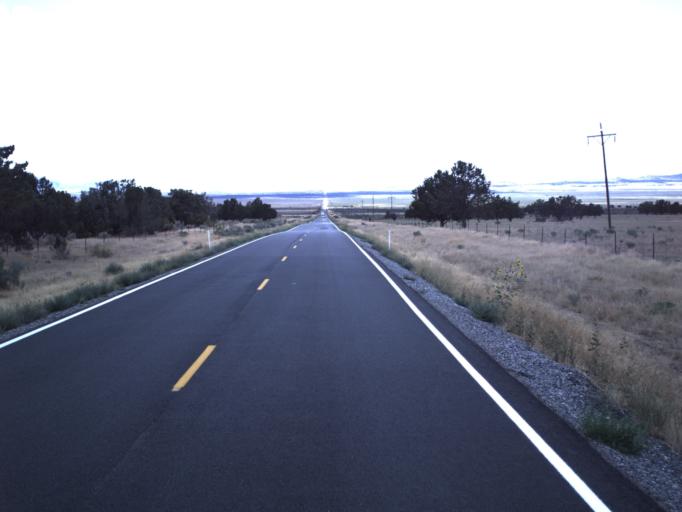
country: US
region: Utah
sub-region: Tooele County
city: Grantsville
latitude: 40.3089
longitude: -112.6397
